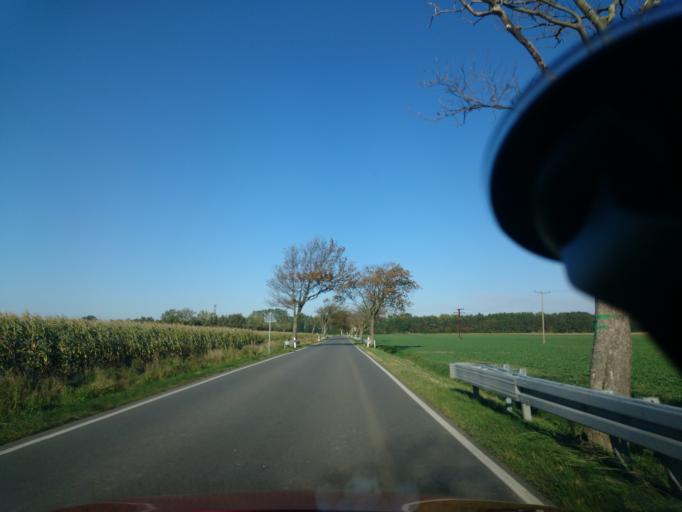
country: DE
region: Mecklenburg-Vorpommern
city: Saal
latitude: 54.3013
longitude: 12.5080
